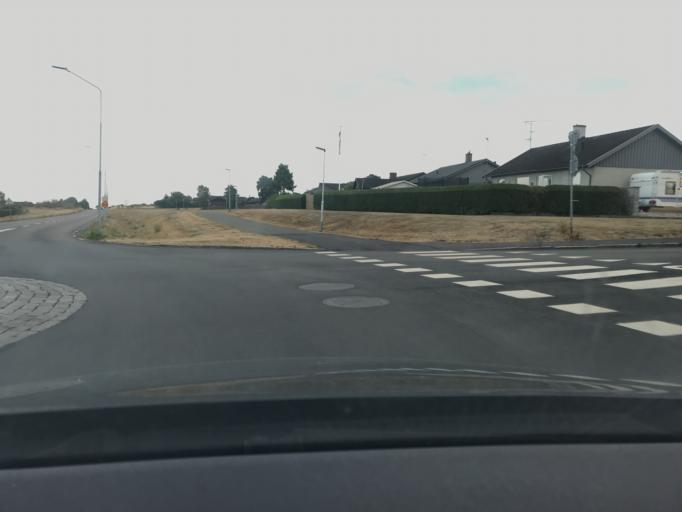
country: SE
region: Skane
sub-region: Simrishamns Kommun
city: Simrishamn
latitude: 55.5457
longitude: 14.3516
